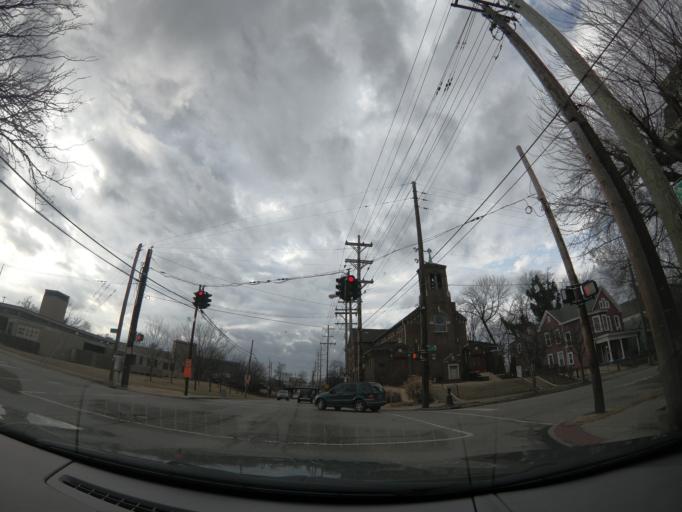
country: US
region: Kentucky
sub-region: Jefferson County
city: Louisville
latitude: 38.2264
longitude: -85.7651
